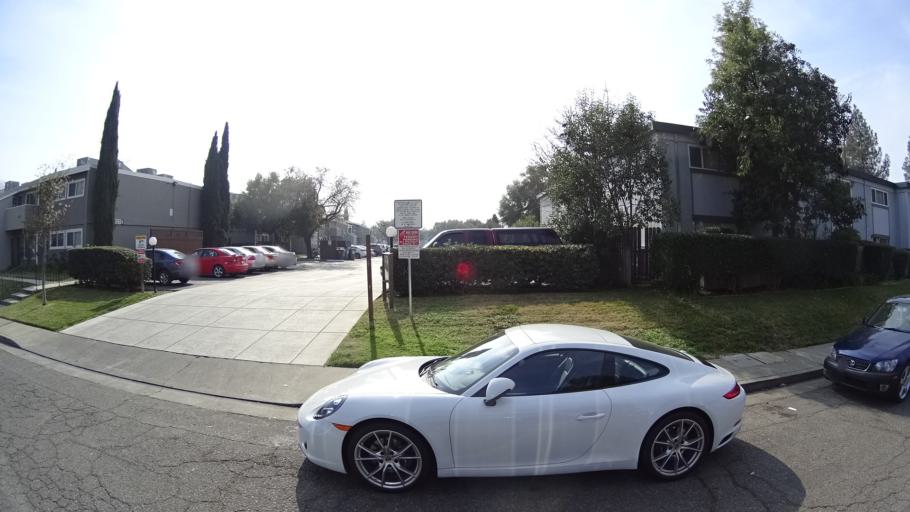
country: US
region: California
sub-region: Yolo County
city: Davis
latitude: 38.5621
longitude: -121.7573
